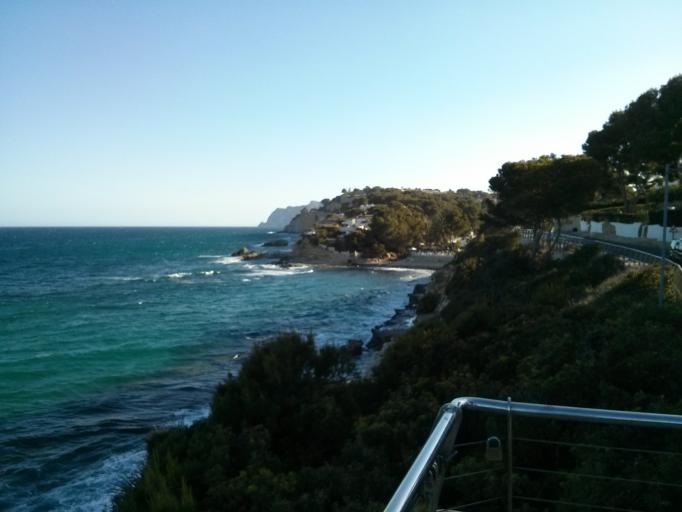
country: ES
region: Valencia
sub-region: Provincia de Alicante
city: Moraira
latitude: 38.6832
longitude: 0.1226
